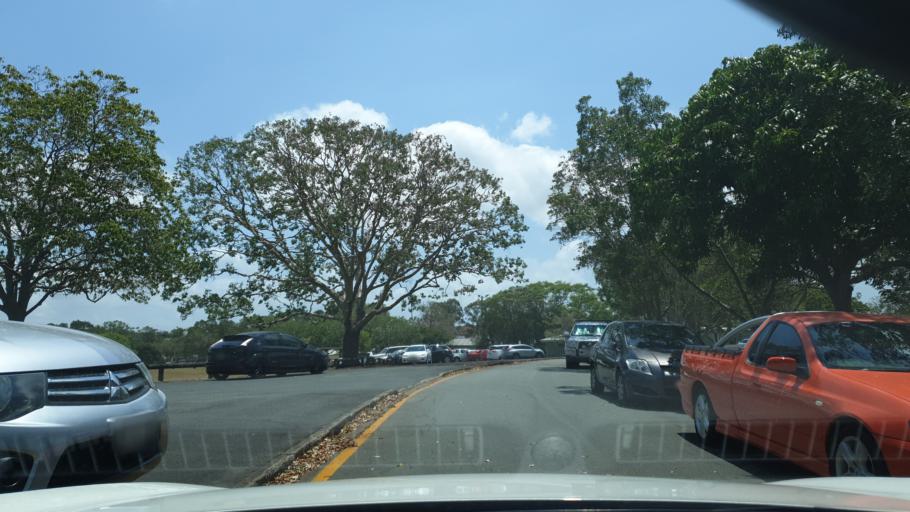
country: AU
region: Queensland
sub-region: Brisbane
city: Chermside West
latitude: -27.3765
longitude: 153.0298
